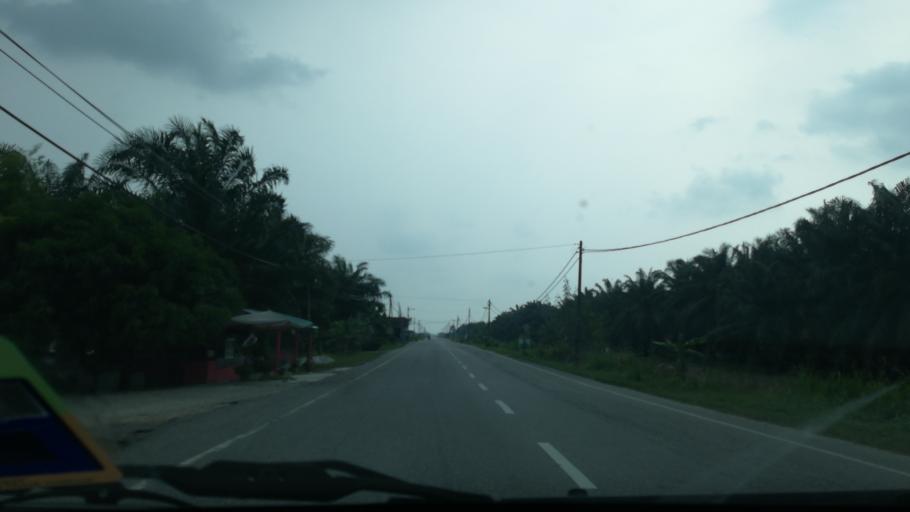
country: MY
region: Perak
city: Teluk Intan
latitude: 4.1121
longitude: 101.0673
